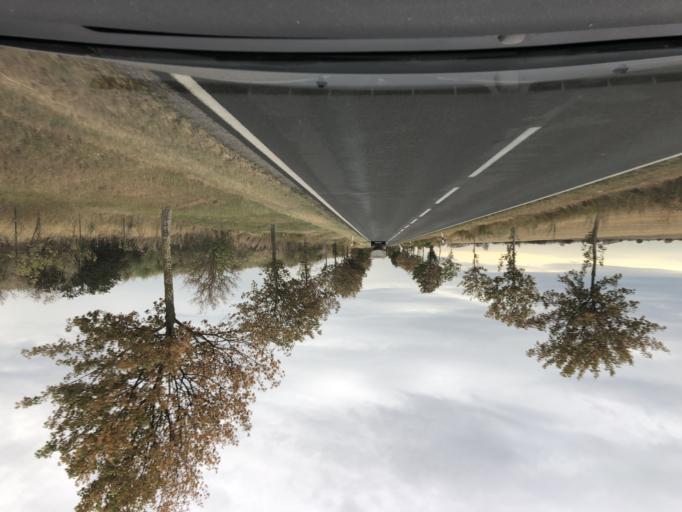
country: DE
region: Saxony-Anhalt
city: Nienburg/Saale
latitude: 51.8431
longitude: 11.7430
